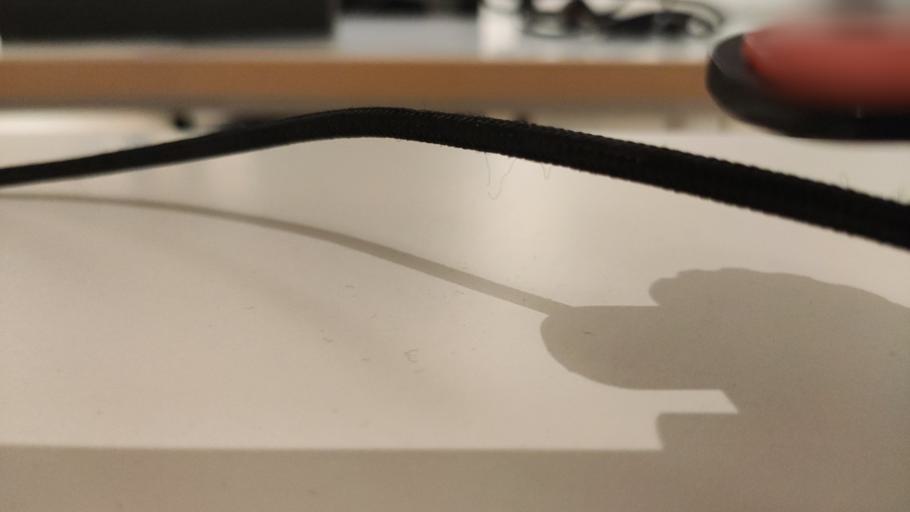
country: RU
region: Moskovskaya
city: Dorokhovo
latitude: 55.3891
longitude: 36.3931
